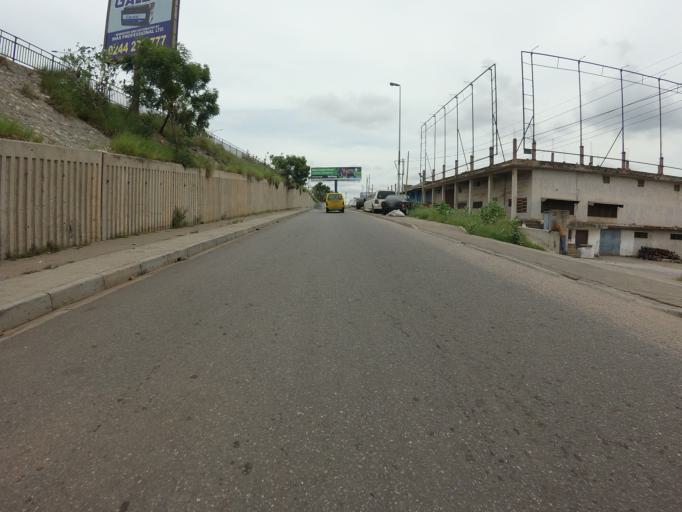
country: GH
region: Greater Accra
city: Accra
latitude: 5.5923
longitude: -0.2196
